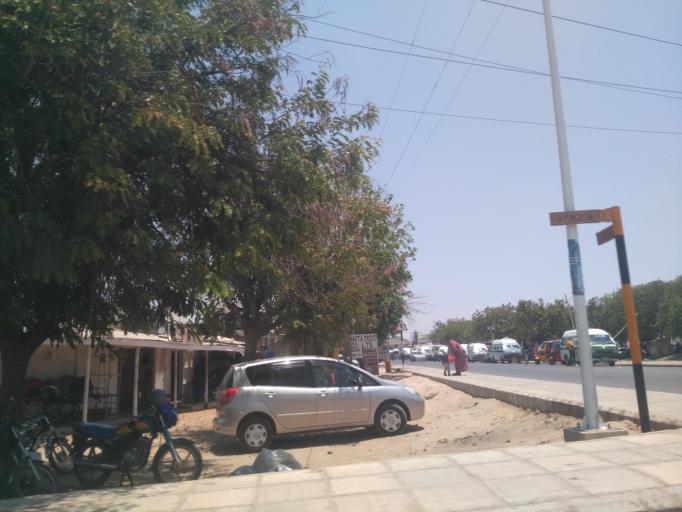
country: TZ
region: Dodoma
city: Dodoma
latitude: -6.1756
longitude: 35.7414
